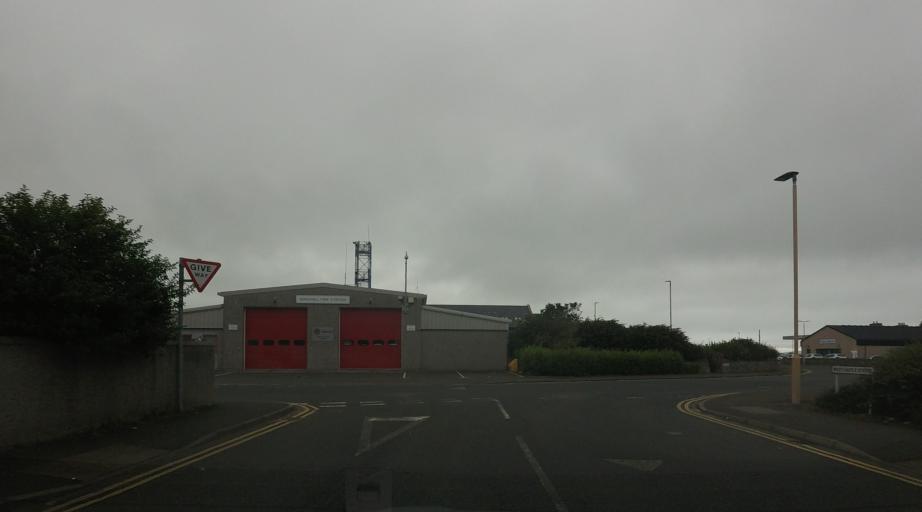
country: GB
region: Scotland
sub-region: Orkney Islands
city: Orkney
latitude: 58.9830
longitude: -2.9626
